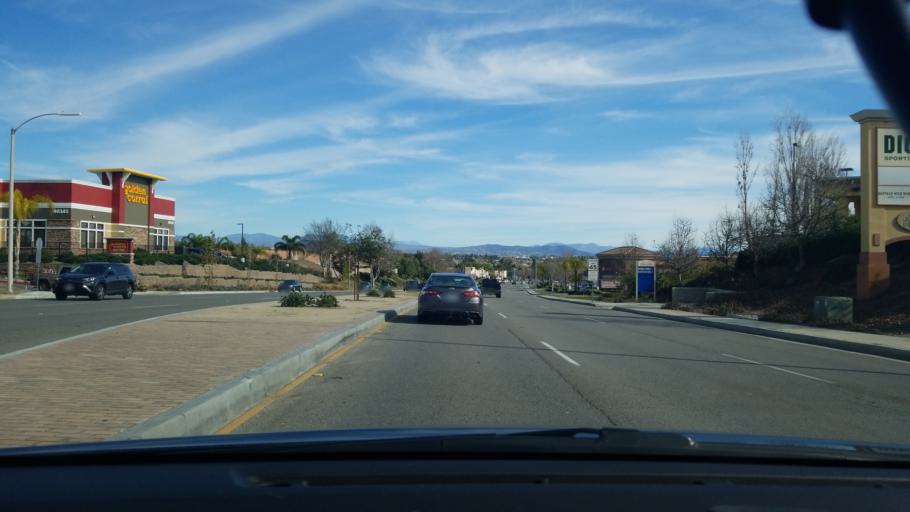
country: US
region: California
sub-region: Riverside County
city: Murrieta Hot Springs
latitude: 33.5564
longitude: -117.1764
